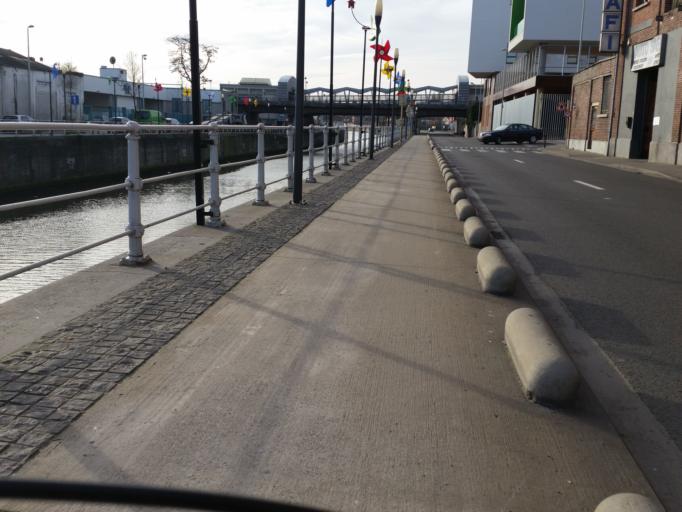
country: BE
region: Brussels Capital
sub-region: Bruxelles-Capitale
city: Brussels
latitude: 50.8460
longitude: 4.3271
